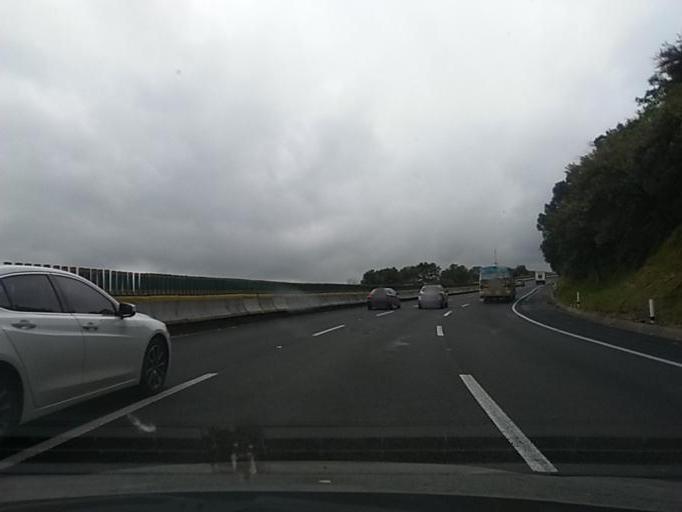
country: MX
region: Mexico City
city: Xochimilco
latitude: 19.2274
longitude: -99.1352
